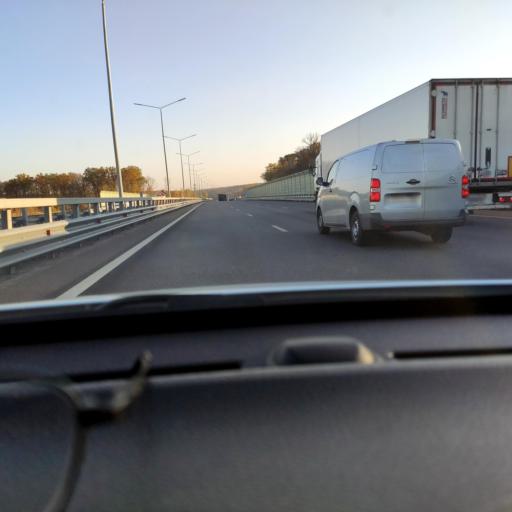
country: RU
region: Voronezj
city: Ramon'
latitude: 51.8176
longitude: 39.2516
